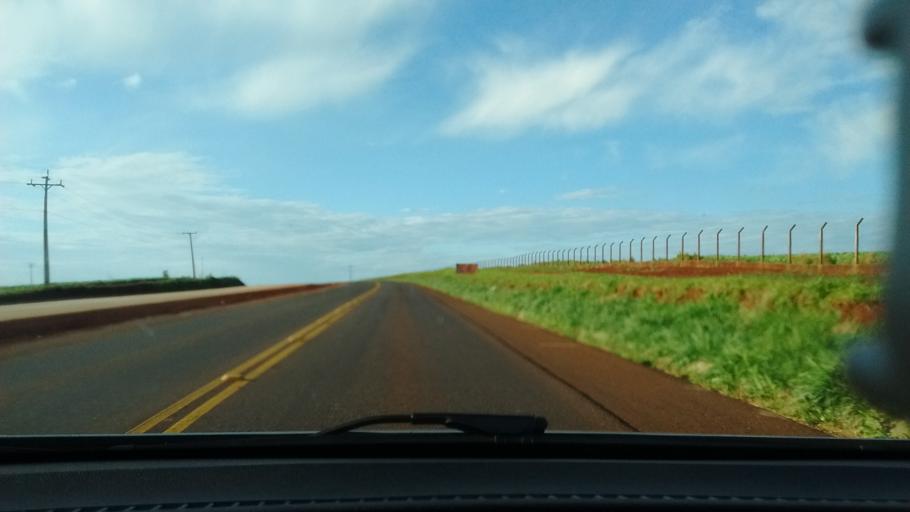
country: BR
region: Parana
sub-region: Cascavel
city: Cascavel
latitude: -25.1254
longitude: -53.5879
